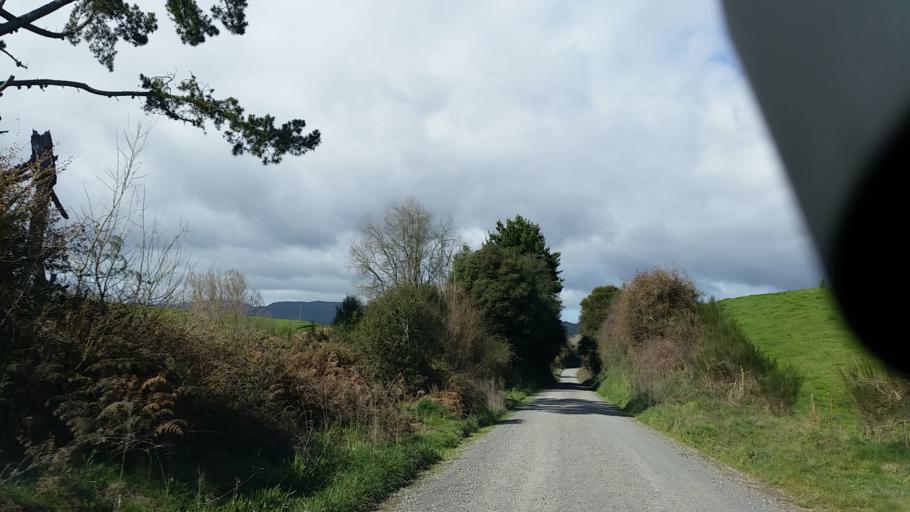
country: NZ
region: Waikato
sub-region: South Waikato District
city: Tokoroa
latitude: -38.3866
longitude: 176.0781
